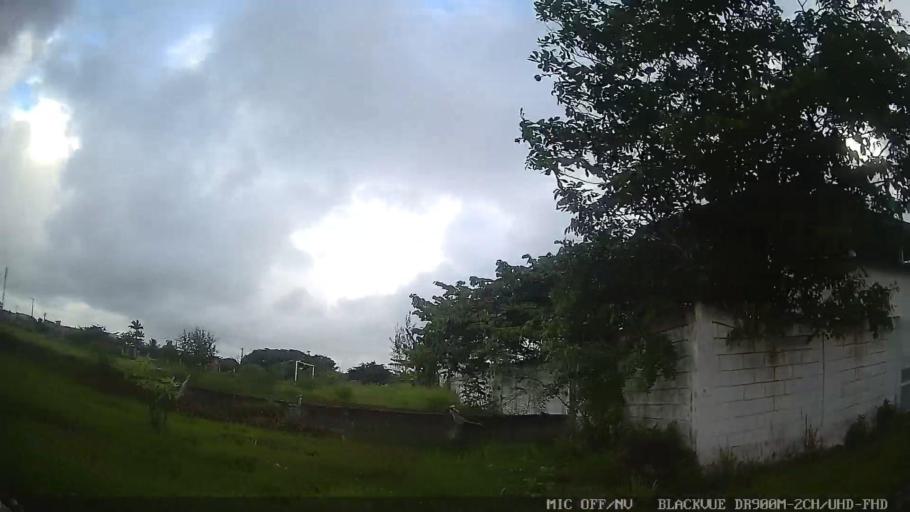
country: BR
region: Sao Paulo
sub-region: Itanhaem
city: Itanhaem
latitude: -24.2060
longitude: -46.8371
